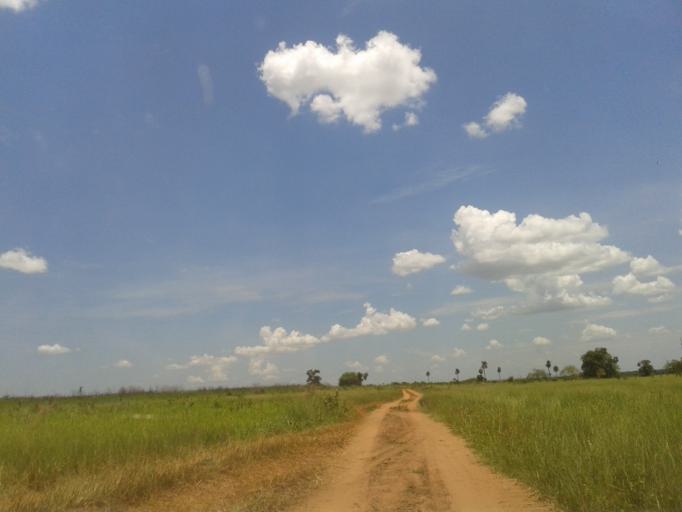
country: BR
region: Minas Gerais
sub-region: Santa Vitoria
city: Santa Vitoria
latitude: -19.2236
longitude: -50.4412
